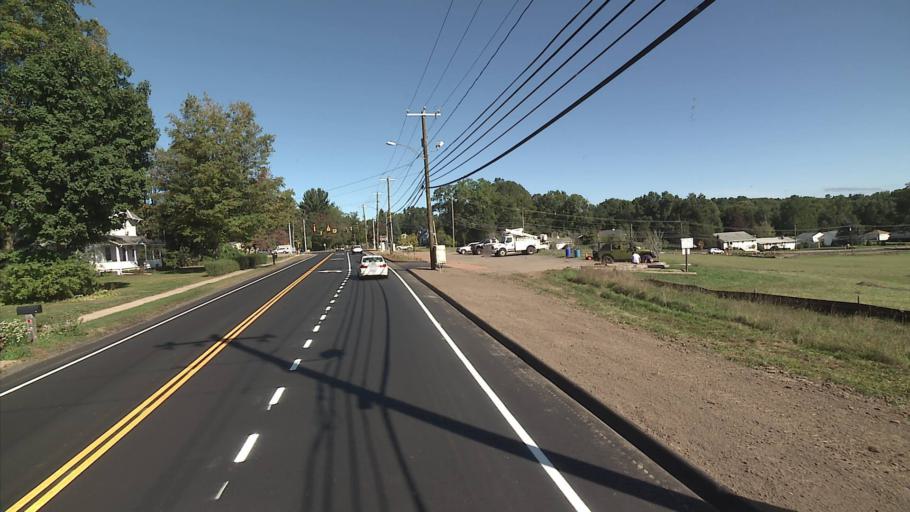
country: US
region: Connecticut
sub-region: Hartford County
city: Bristol
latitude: 41.7029
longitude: -72.9468
